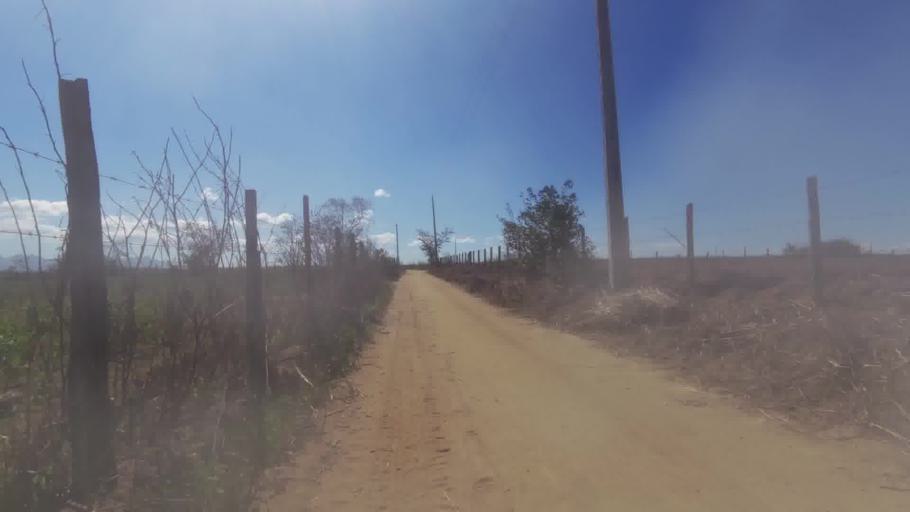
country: BR
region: Espirito Santo
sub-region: Marataizes
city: Marataizes
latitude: -21.1567
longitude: -40.9657
